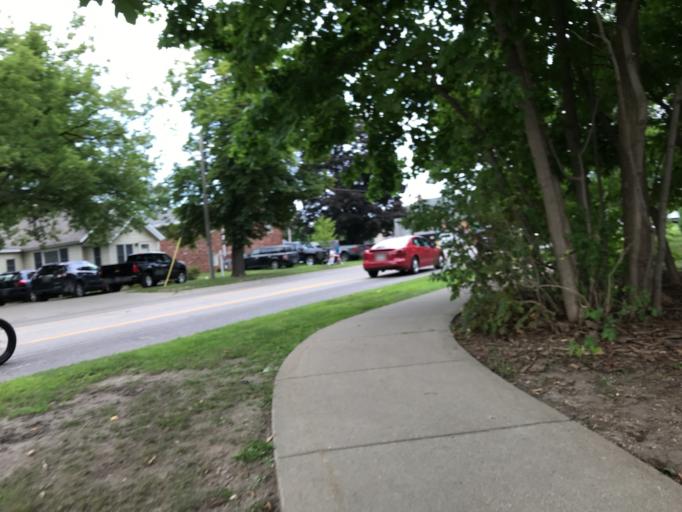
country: US
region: Michigan
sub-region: Oakland County
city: Milford
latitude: 42.5852
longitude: -83.6024
